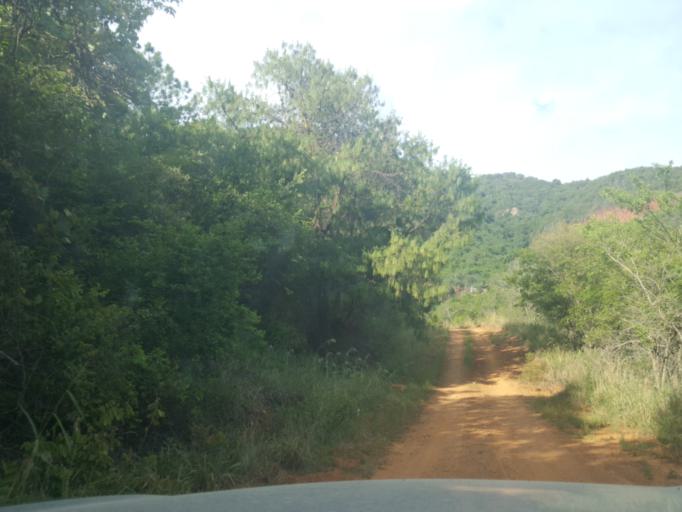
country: ZA
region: Limpopo
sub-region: Mopani District Municipality
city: Hoedspruit
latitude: -24.5923
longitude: 30.8411
